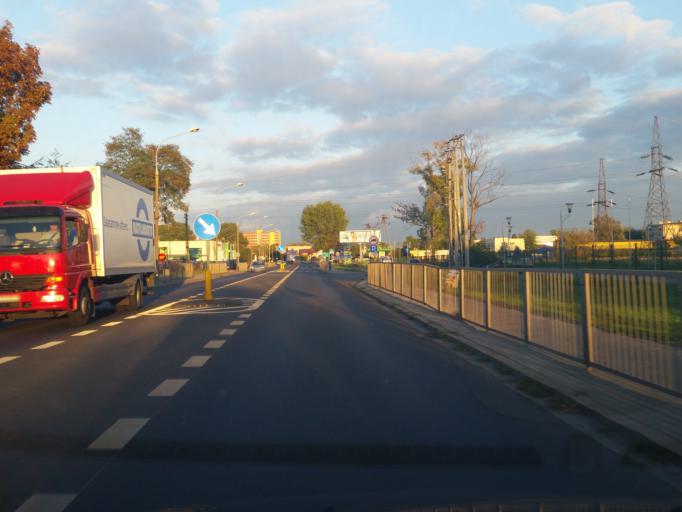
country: PL
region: Masovian Voivodeship
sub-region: Powiat warszawski zachodni
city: Ozarow Mazowiecki
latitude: 52.2101
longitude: 20.8057
